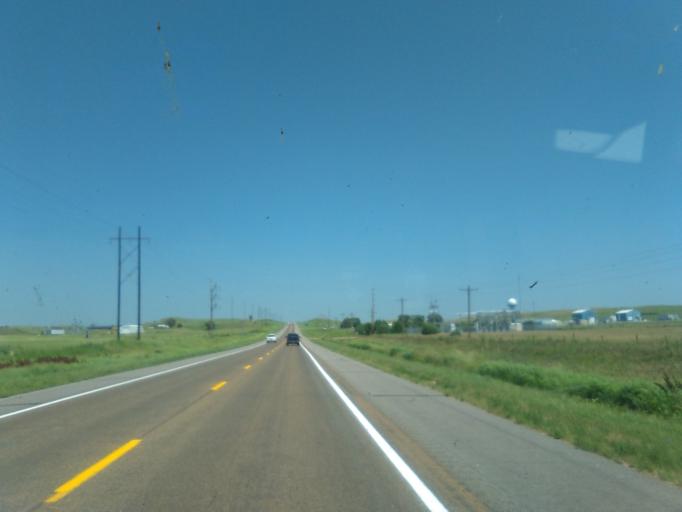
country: US
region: Nebraska
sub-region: Lincoln County
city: North Platte
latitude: 40.8200
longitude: -100.7537
